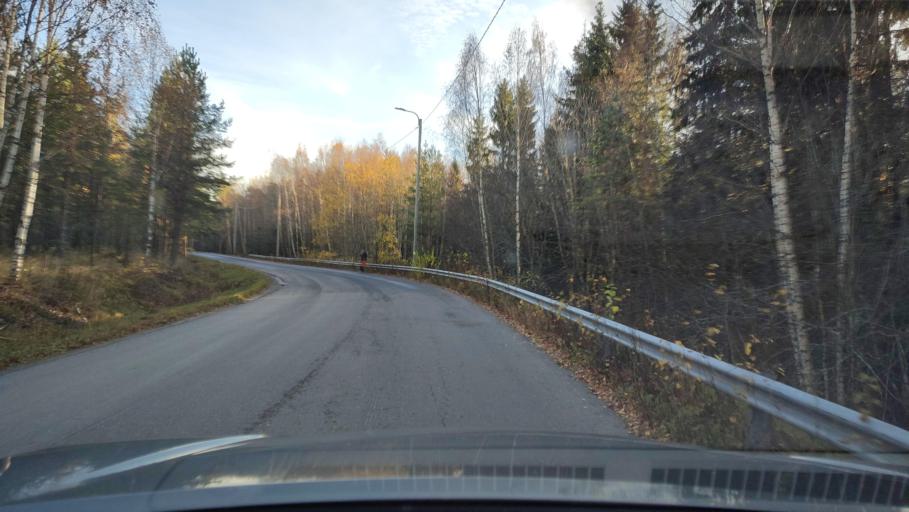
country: FI
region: Ostrobothnia
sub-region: Vaasa
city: Teeriniemi
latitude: 63.0679
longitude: 21.6905
